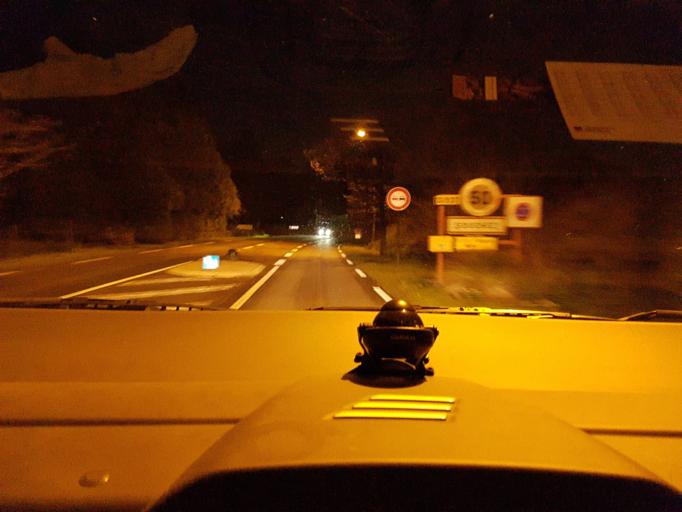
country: FR
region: Nord-Pas-de-Calais
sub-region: Departement du Pas-de-Calais
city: Souchez
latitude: 50.3810
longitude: 2.7419
